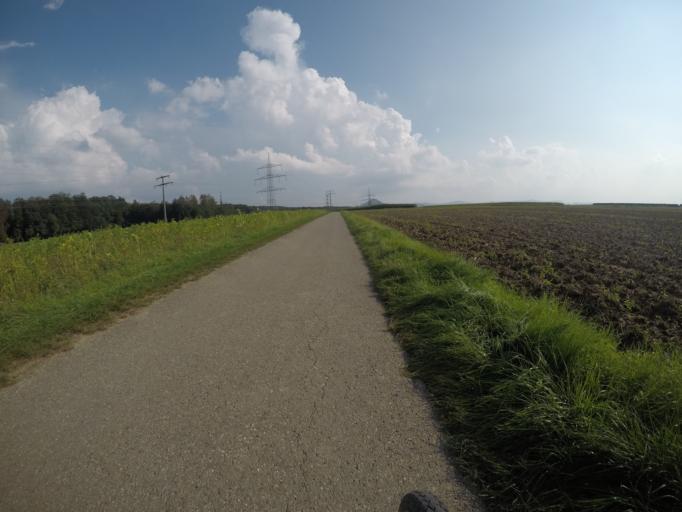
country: DE
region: Baden-Wuerttemberg
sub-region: Tuebingen Region
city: Riederich
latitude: 48.5496
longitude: 9.2387
